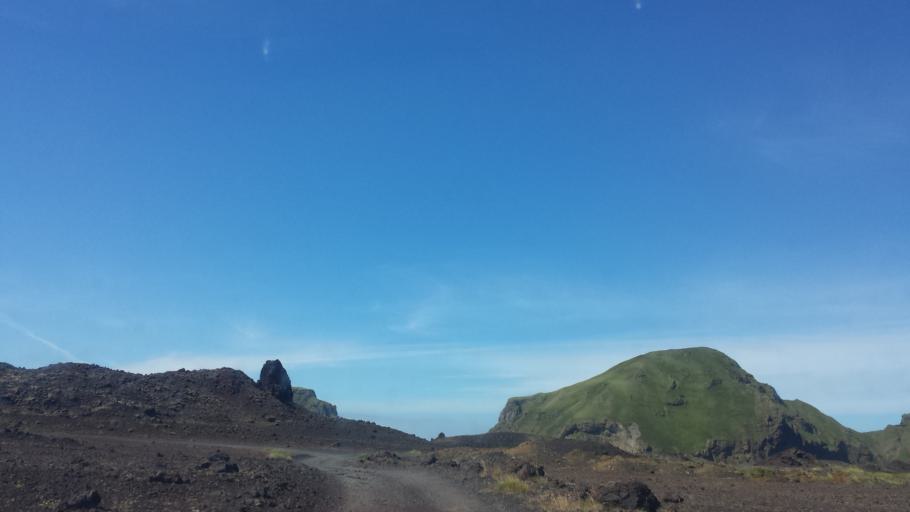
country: IS
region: South
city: Vestmannaeyjar
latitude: 63.4375
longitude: -20.2437
